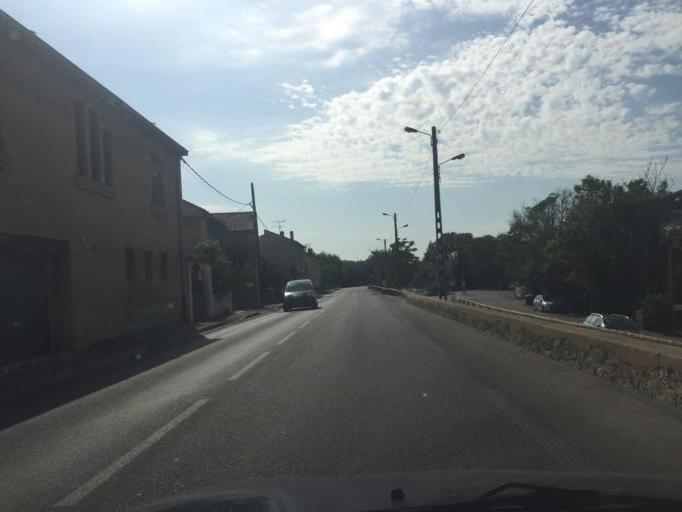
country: FR
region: Provence-Alpes-Cote d'Azur
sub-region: Departement du Vaucluse
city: Apt
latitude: 43.8771
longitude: 5.4085
